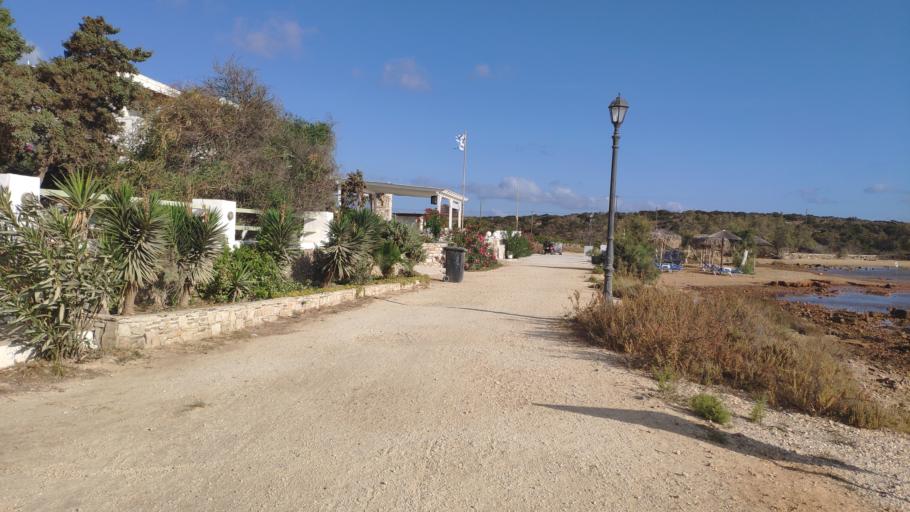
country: GR
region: South Aegean
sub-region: Nomos Kykladon
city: Antiparos
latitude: 37.0431
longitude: 25.0853
